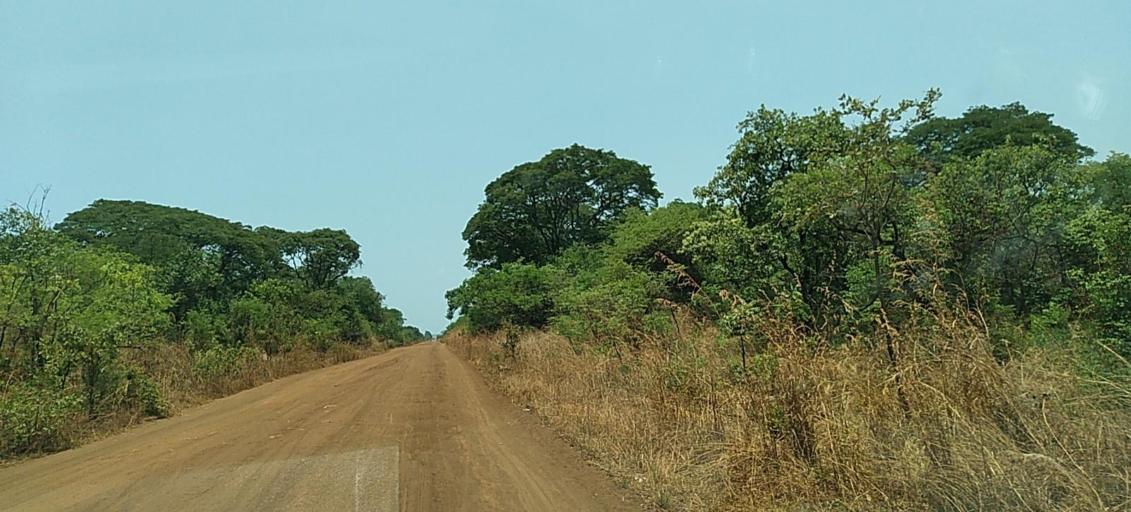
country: ZM
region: Copperbelt
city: Mpongwe
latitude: -13.6888
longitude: 27.8611
